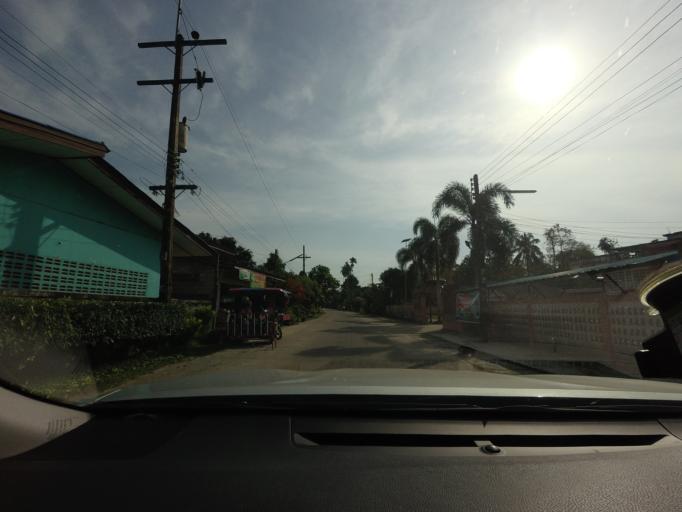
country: TH
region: Narathiwat
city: Ra-ngae
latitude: 6.3093
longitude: 101.7779
